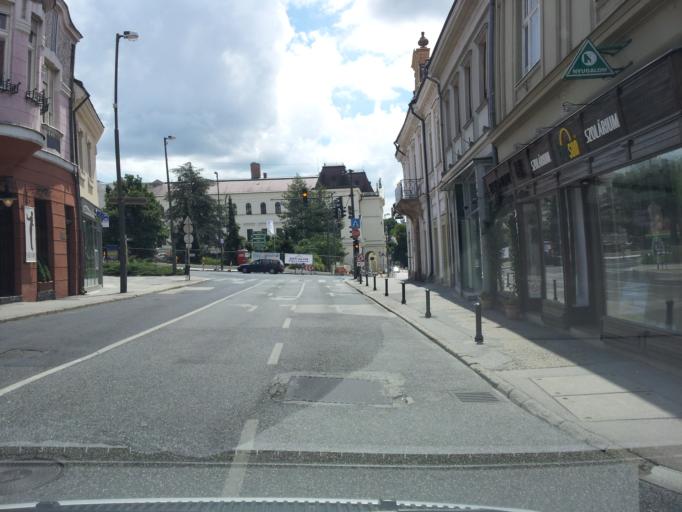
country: HU
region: Veszprem
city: Veszprem
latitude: 47.0931
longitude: 17.9076
